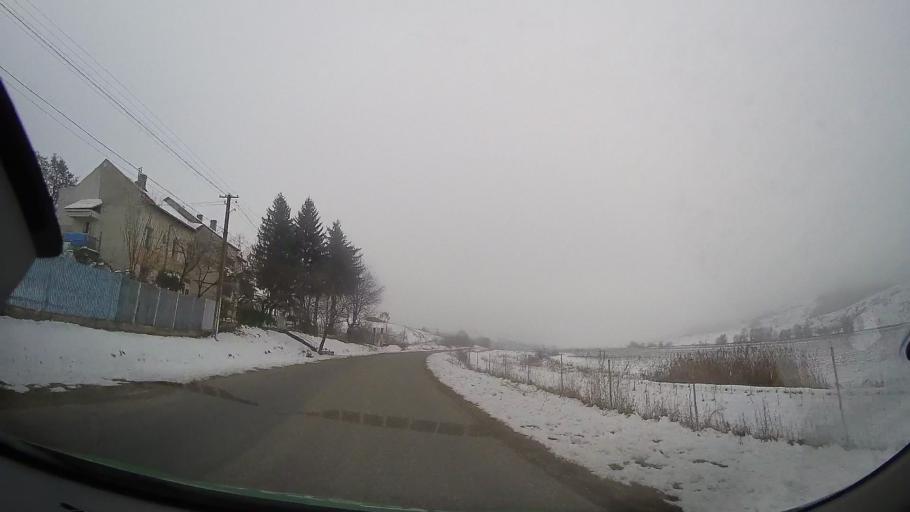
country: RO
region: Bacau
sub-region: Comuna Vultureni
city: Vultureni
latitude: 46.3663
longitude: 27.2850
